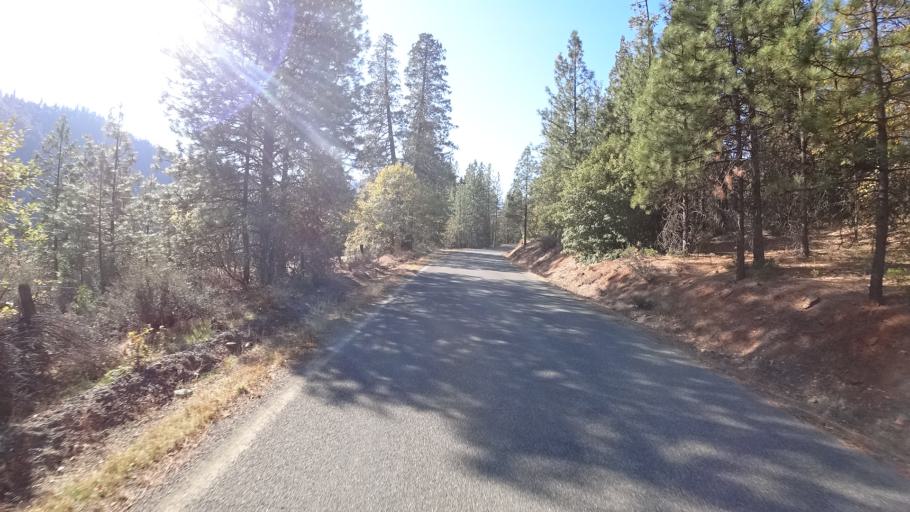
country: US
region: California
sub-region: Siskiyou County
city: Yreka
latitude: 41.7343
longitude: -123.0067
